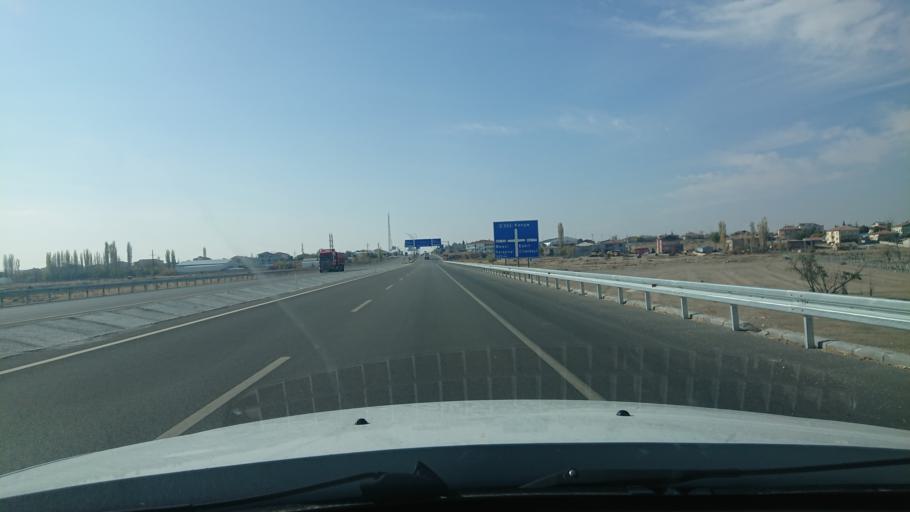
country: TR
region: Aksaray
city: Sultanhani
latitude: 38.2491
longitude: 33.4547
